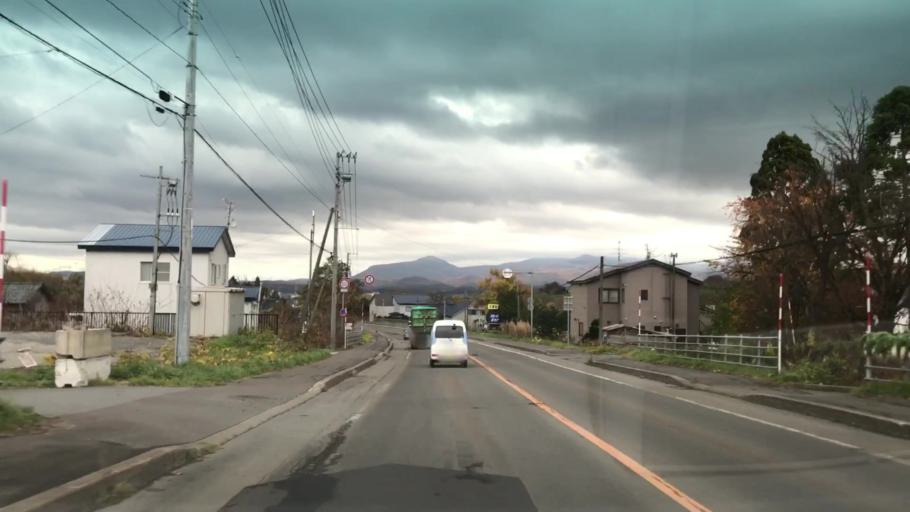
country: JP
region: Hokkaido
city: Yoichi
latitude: 43.2105
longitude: 140.7542
